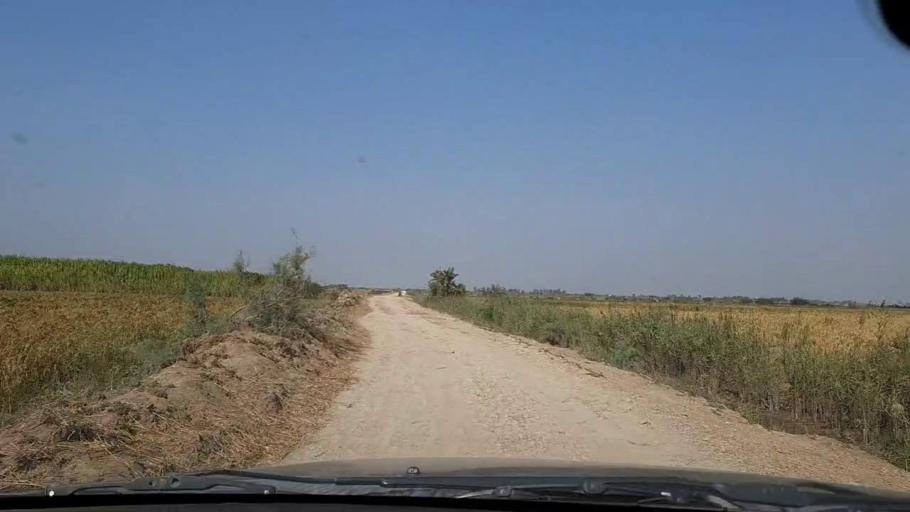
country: PK
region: Sindh
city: Mirpur Sakro
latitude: 24.3654
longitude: 67.6830
